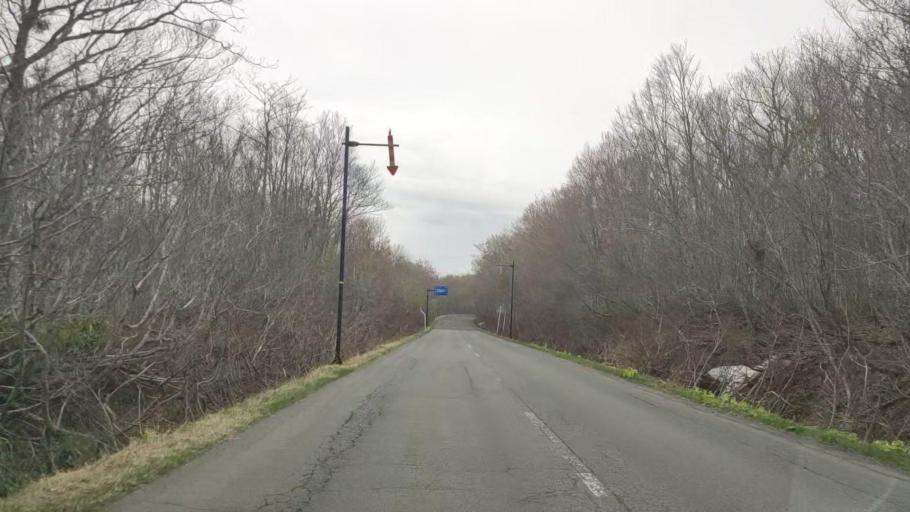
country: JP
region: Aomori
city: Aomori Shi
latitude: 40.6634
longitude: 140.9591
